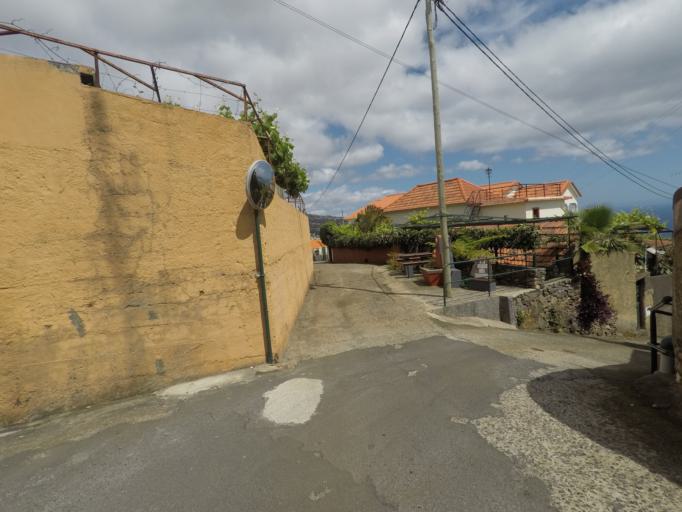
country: PT
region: Madeira
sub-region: Calheta
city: Estreito da Calheta
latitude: 32.7355
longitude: -17.1865
